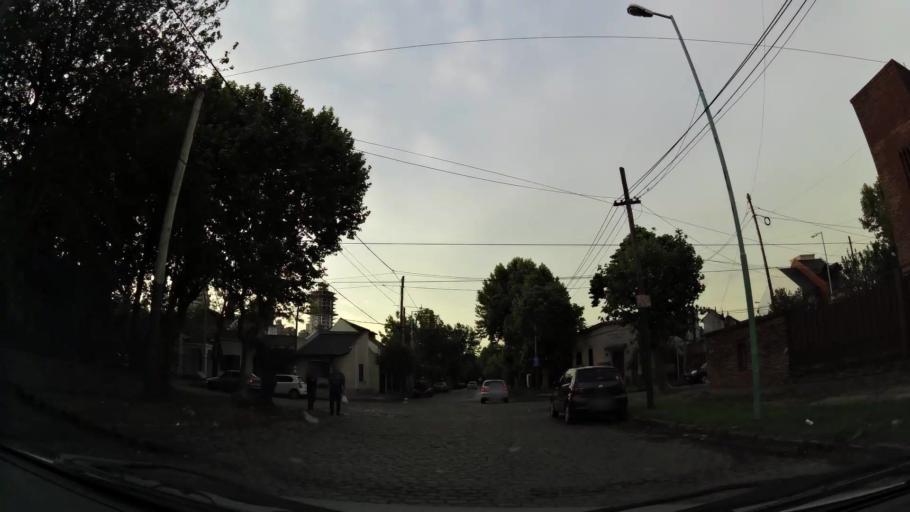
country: AR
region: Buenos Aires
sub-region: Partido de Lomas de Zamora
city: Lomas de Zamora
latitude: -34.7692
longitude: -58.3940
